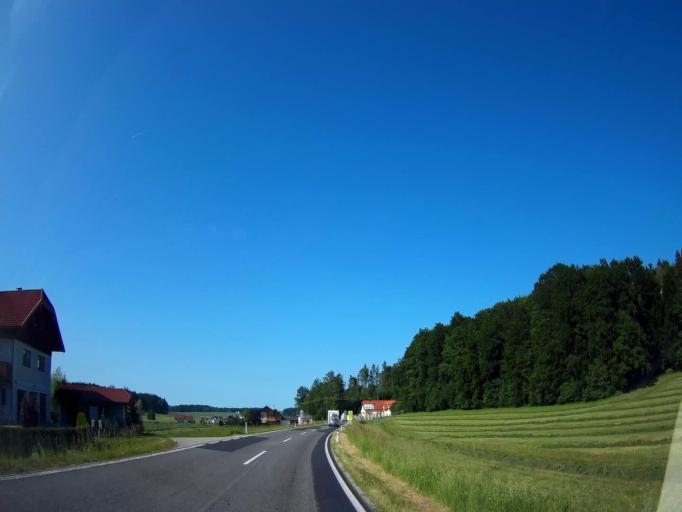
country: AT
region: Salzburg
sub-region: Politischer Bezirk Salzburg-Umgebung
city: Dorfbeuern
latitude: 48.1047
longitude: 12.9974
